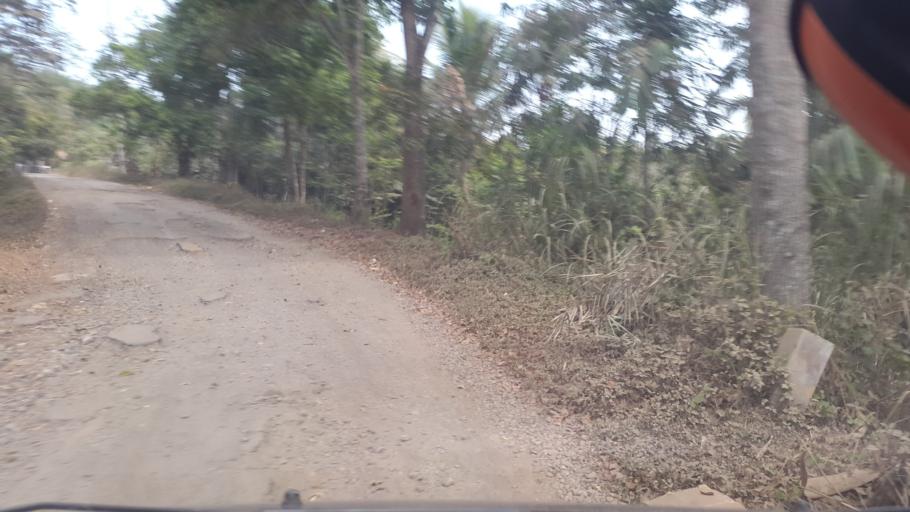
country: ID
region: West Java
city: Cisireum
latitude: -7.1165
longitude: 106.6428
